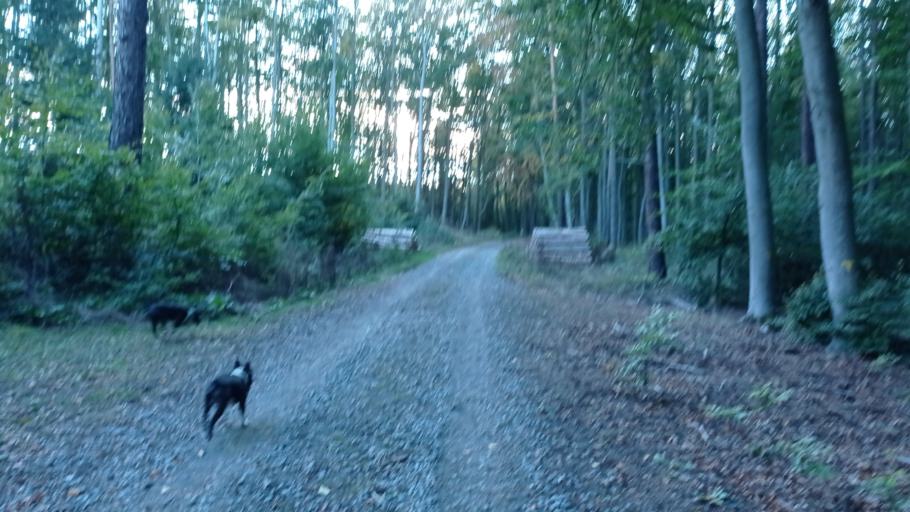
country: CZ
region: Central Bohemia
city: Chynava
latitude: 50.0541
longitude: 14.0478
